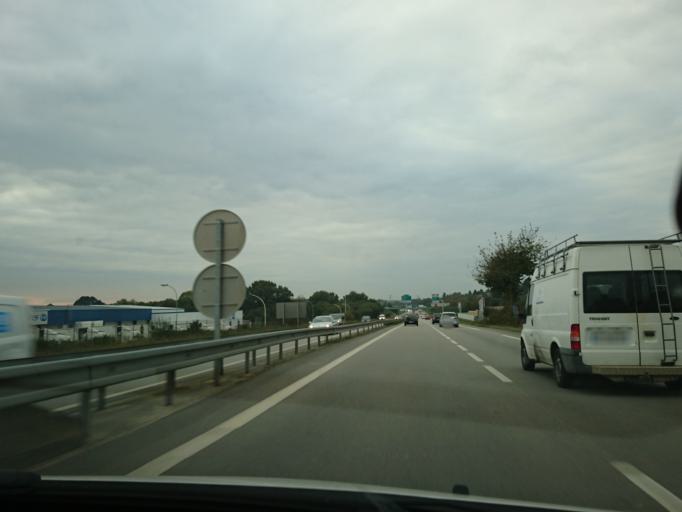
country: FR
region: Brittany
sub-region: Departement du Morbihan
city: Vannes
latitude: 47.6643
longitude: -2.7195
